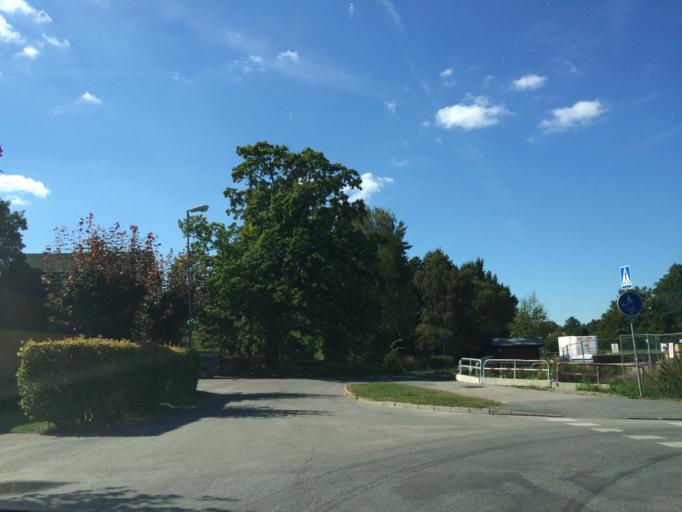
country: SE
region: Stockholm
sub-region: Sollentuna Kommun
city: Sollentuna
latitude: 59.4562
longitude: 17.9091
